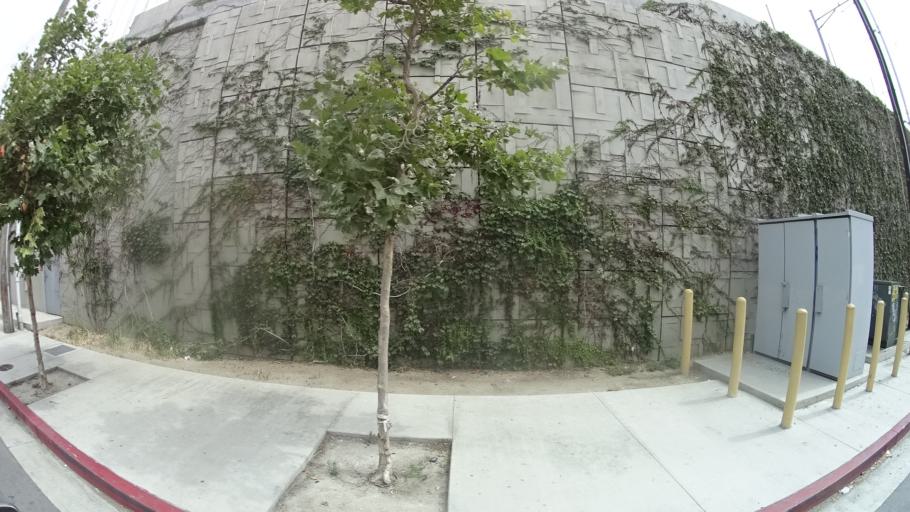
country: US
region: California
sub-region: Los Angeles County
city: View Park-Windsor Hills
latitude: 34.0246
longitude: -118.3540
